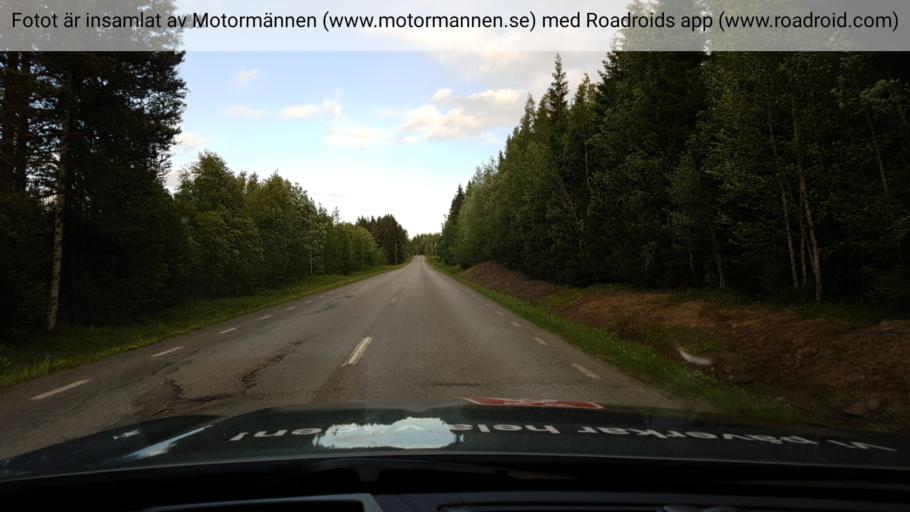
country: SE
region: Jaemtland
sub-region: Krokoms Kommun
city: Krokom
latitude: 63.1557
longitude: 14.1449
